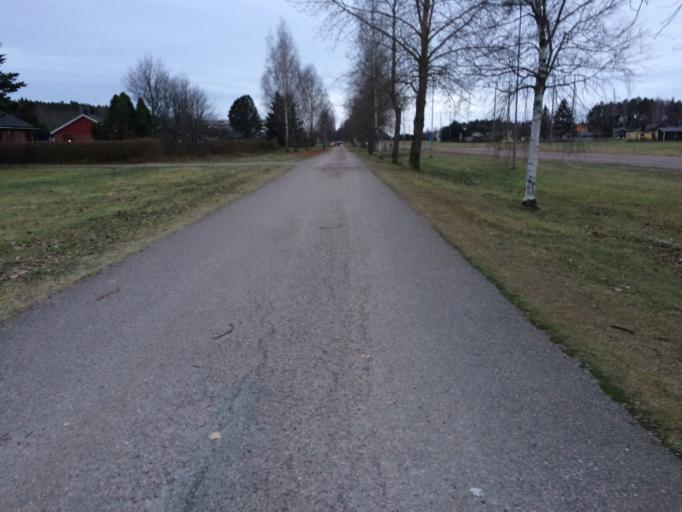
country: SE
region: Vaestmanland
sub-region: Hallstahammars Kommun
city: Hallstahammar
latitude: 59.6208
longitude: 16.2539
